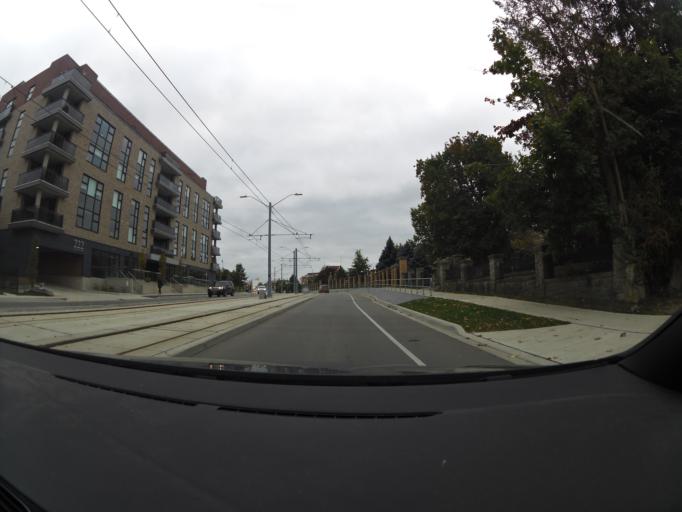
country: CA
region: Ontario
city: Waterloo
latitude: 43.4591
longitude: -80.5173
